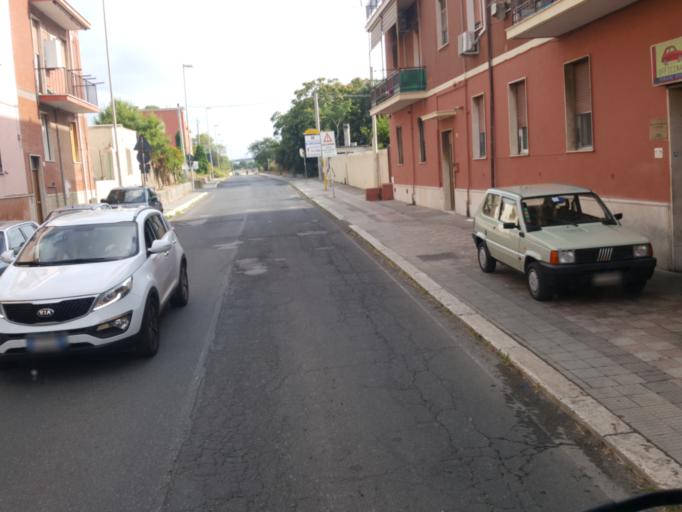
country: IT
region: Latium
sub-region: Citta metropolitana di Roma Capitale
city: Civitavecchia
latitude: 42.1005
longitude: 11.7920
